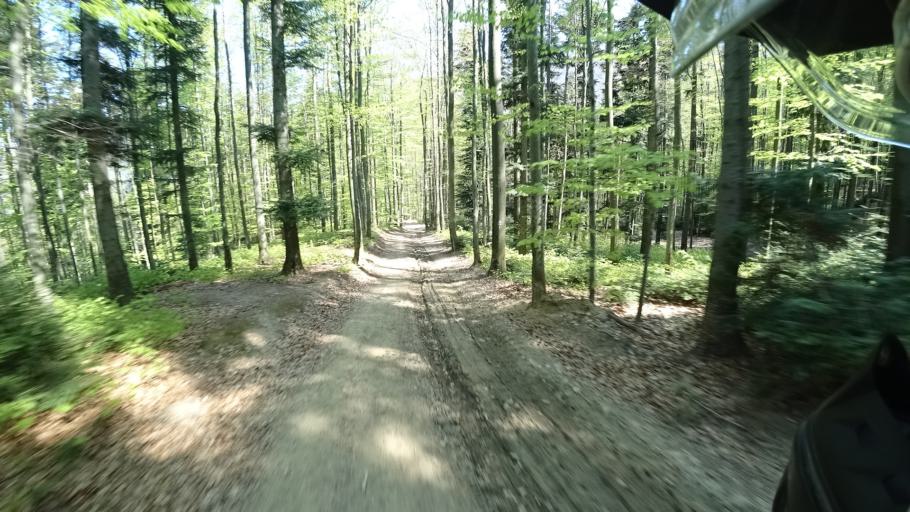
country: HR
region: Zagrebacka
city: Jablanovec
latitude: 45.9002
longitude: 15.9211
